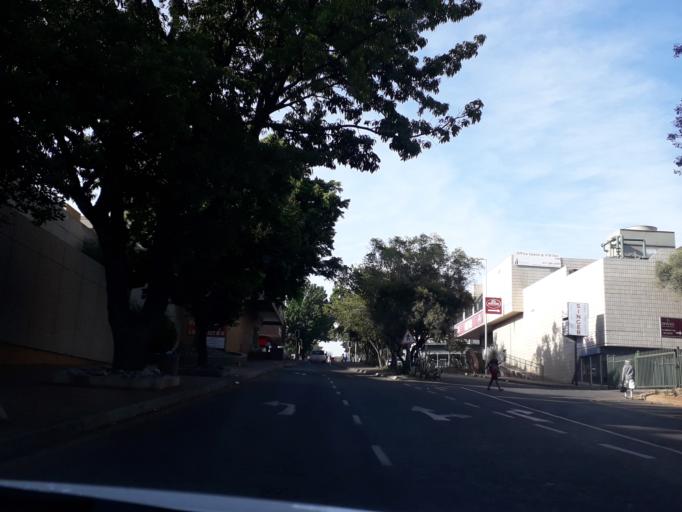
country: ZA
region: Gauteng
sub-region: City of Johannesburg Metropolitan Municipality
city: Johannesburg
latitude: -26.0921
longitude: 28.0025
